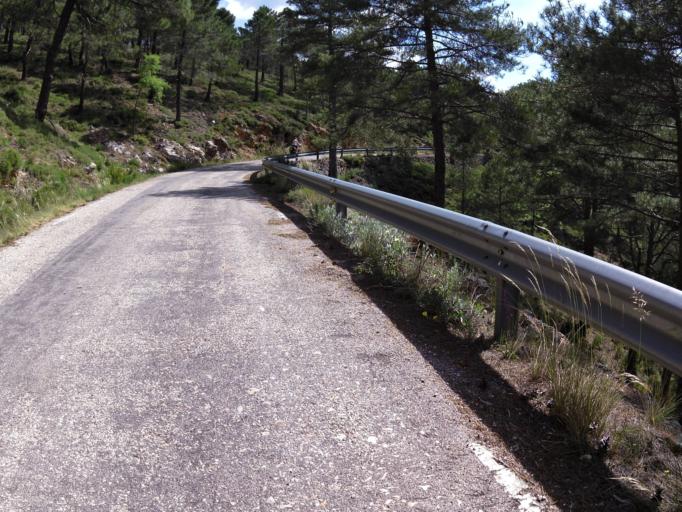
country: ES
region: Castille-La Mancha
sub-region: Provincia de Albacete
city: Riopar
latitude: 38.5270
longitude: -2.4268
